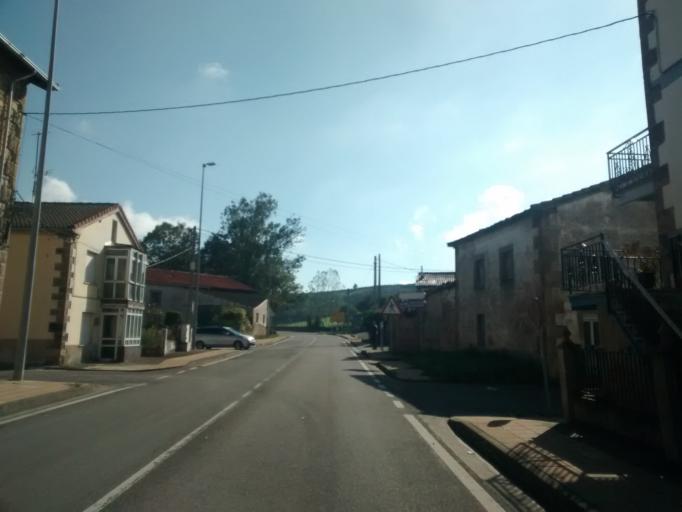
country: ES
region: Cantabria
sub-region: Provincia de Cantabria
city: Reinosa
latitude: 42.9899
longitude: -4.1250
